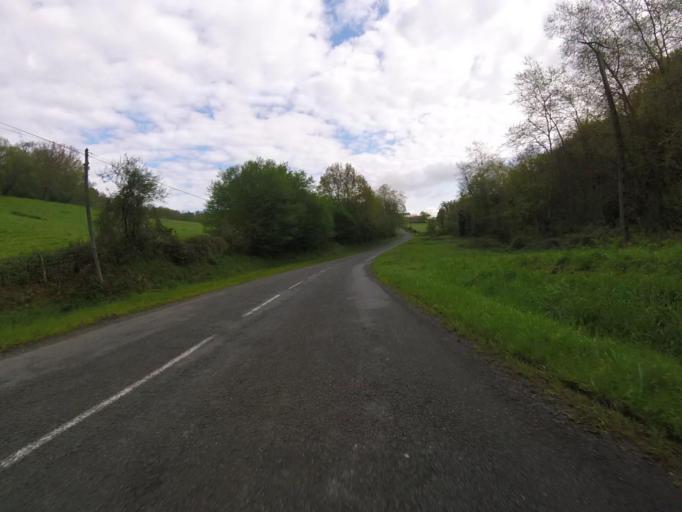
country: FR
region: Aquitaine
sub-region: Departement des Pyrenees-Atlantiques
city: Sare
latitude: 43.2945
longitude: -1.5926
